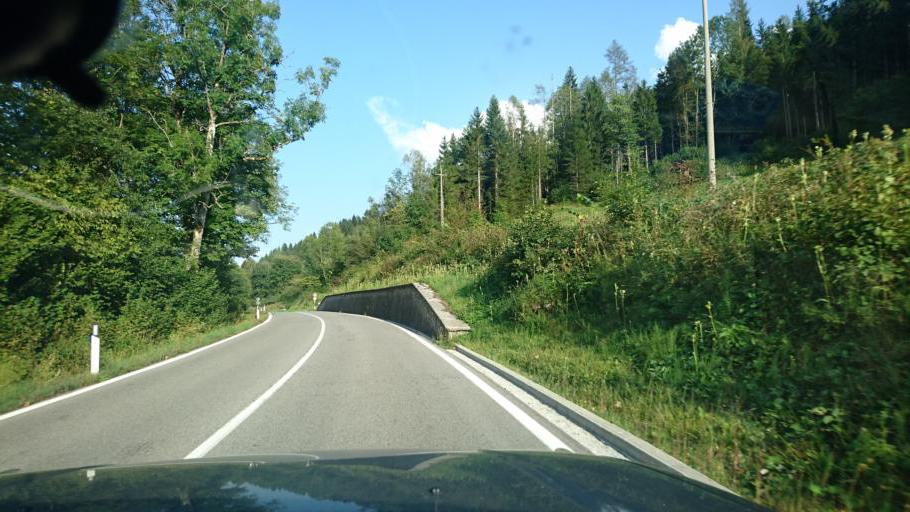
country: AT
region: Carinthia
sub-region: Politischer Bezirk Villach Land
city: Hohenthurn
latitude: 46.4949
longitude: 13.6524
